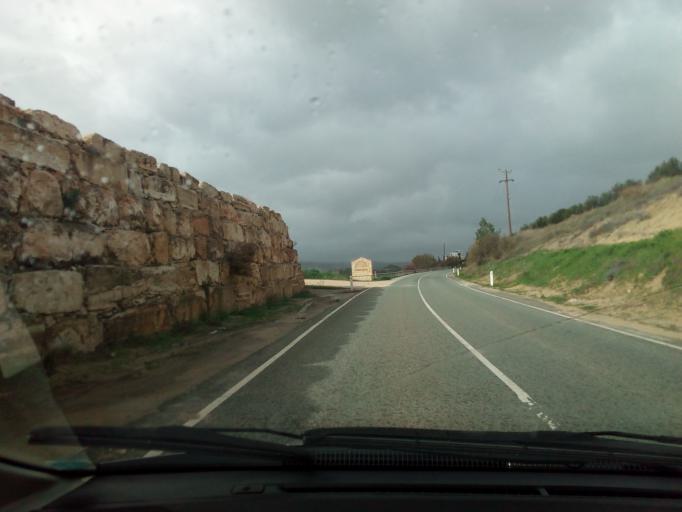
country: CY
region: Pafos
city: Polis
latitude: 34.9530
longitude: 32.4843
